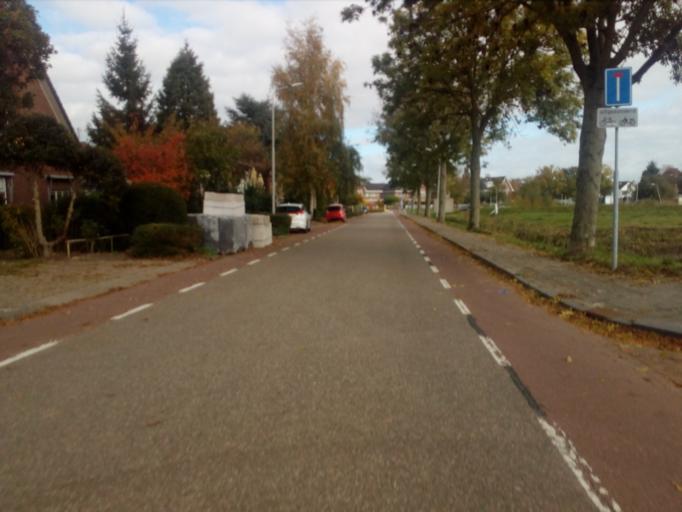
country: NL
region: South Holland
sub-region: Gemeente Lansingerland
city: Berkel en Rodenrijs
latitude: 51.9977
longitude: 4.4779
